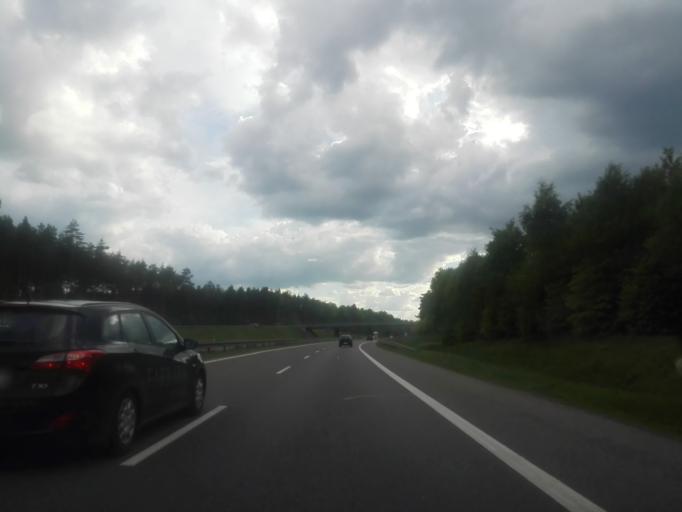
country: PL
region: Masovian Voivodeship
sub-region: Powiat ostrowski
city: Ostrow Mazowiecka
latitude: 52.7862
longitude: 21.8619
